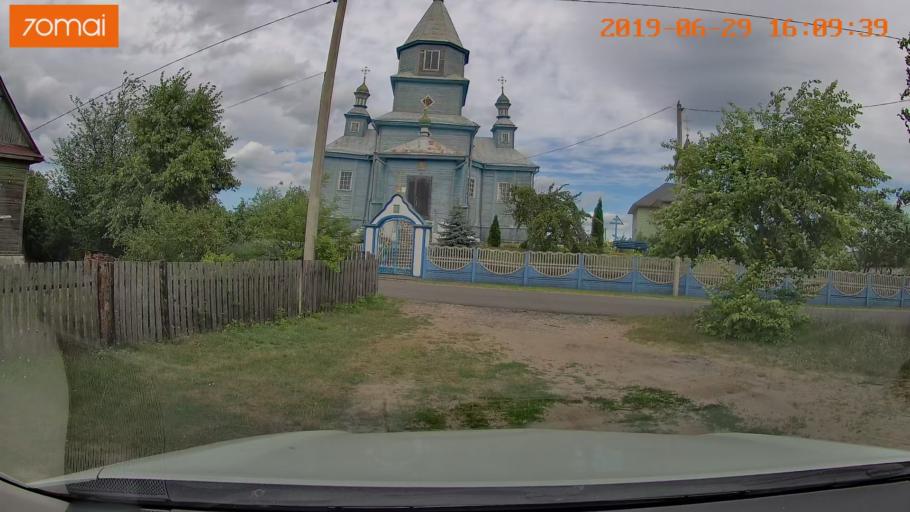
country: BY
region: Brest
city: Luninyets
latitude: 52.2051
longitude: 27.0098
